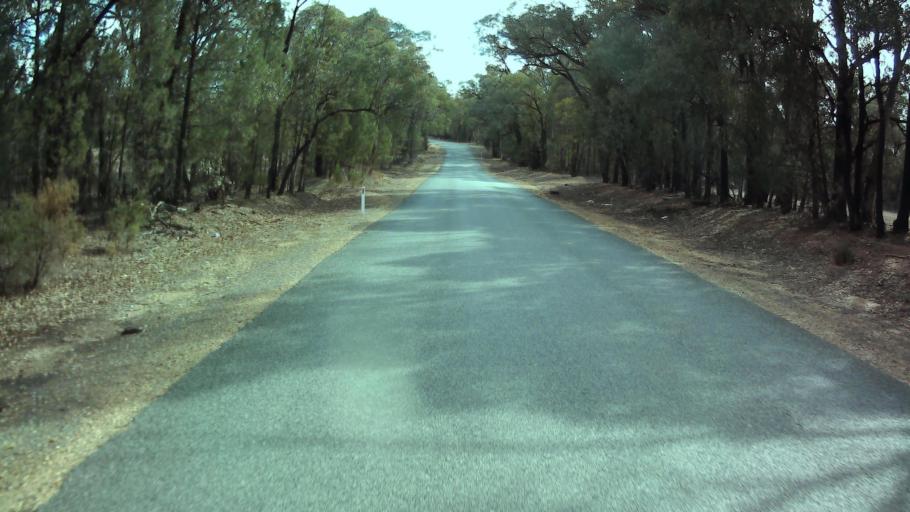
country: AU
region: New South Wales
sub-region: Weddin
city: Grenfell
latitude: -33.8907
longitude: 148.1929
